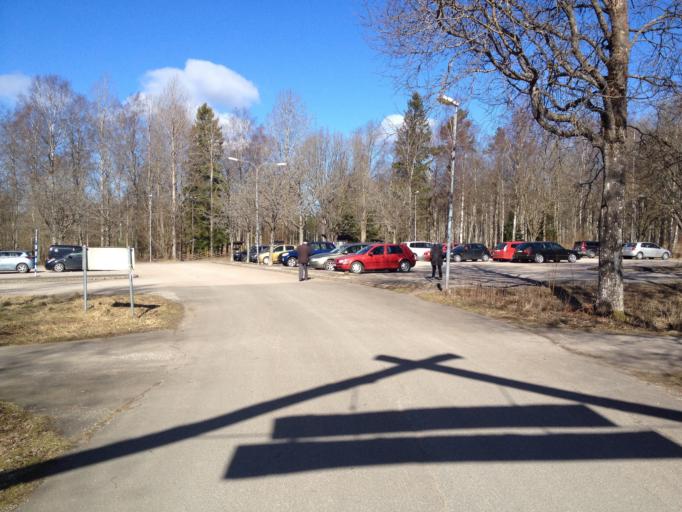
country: SE
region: Vaestra Goetaland
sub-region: Falkopings Kommun
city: Falkoeping
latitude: 58.1769
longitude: 13.5276
